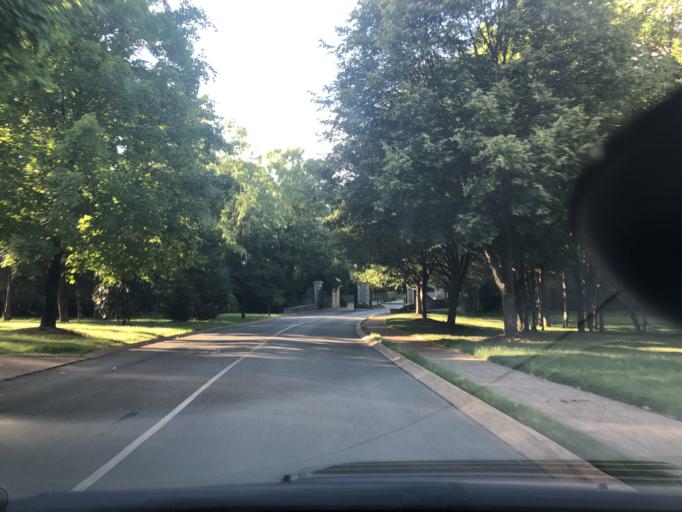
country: US
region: Tennessee
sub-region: Davidson County
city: Forest Hills
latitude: 36.0585
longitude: -86.8347
